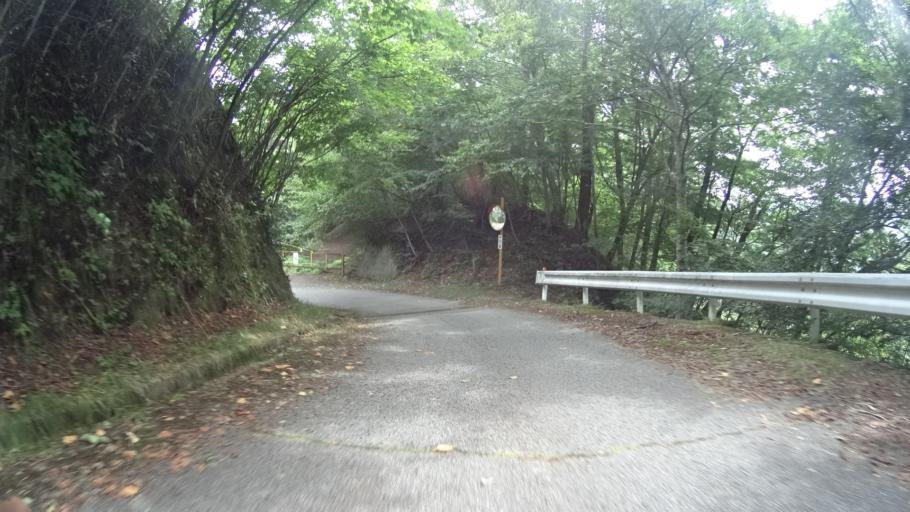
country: JP
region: Yamanashi
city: Kofu-shi
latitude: 35.8273
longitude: 138.5800
